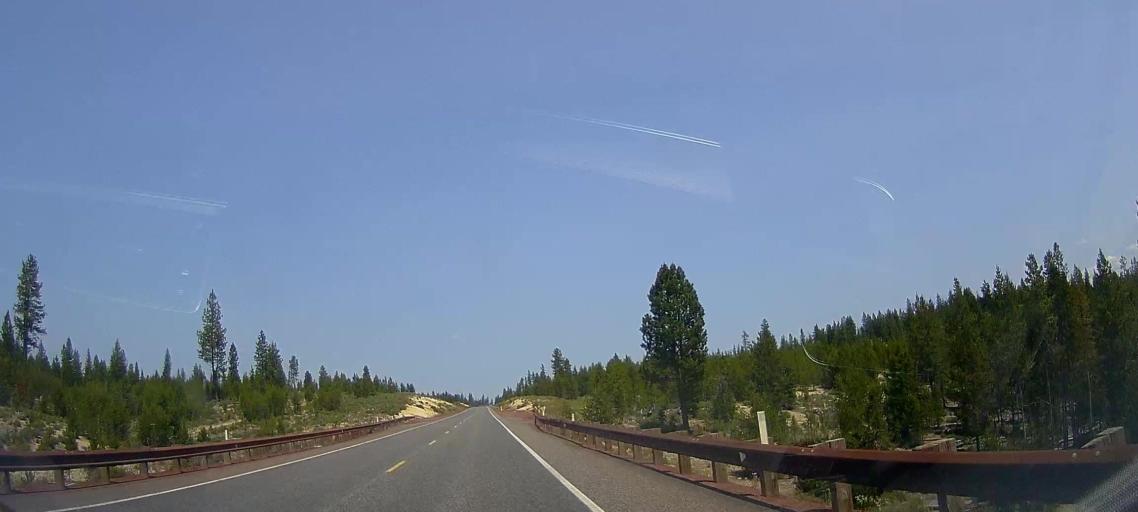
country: US
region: Oregon
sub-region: Deschutes County
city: La Pine
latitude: 43.4002
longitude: -121.7252
